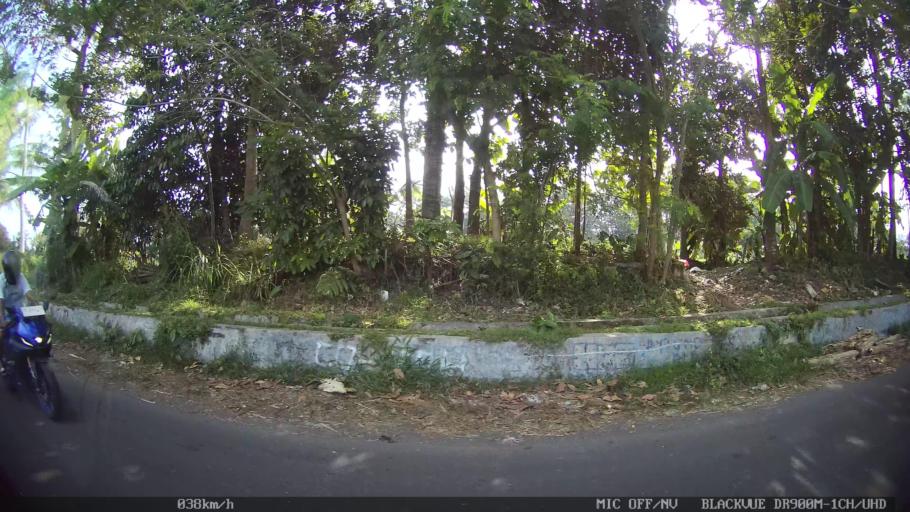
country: ID
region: Daerah Istimewa Yogyakarta
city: Depok
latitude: -7.7237
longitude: 110.4392
